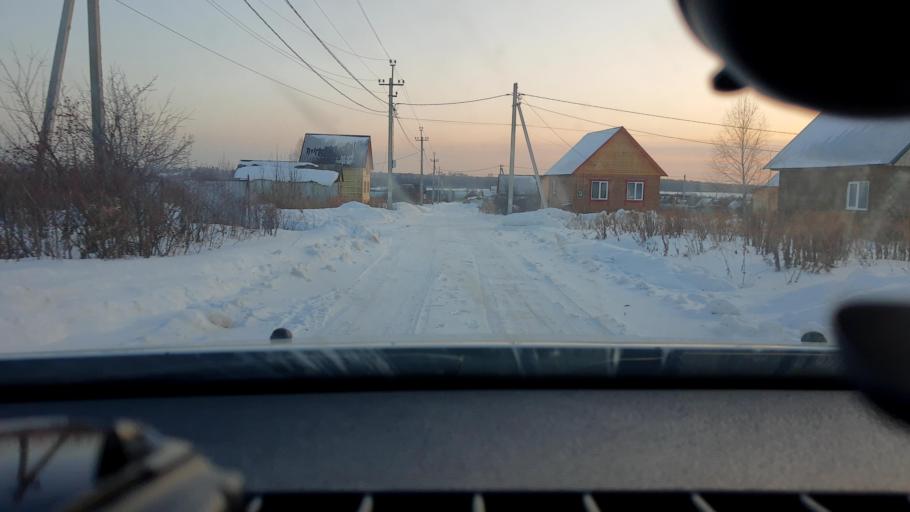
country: RU
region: Bashkortostan
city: Iglino
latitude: 54.8624
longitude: 56.4803
